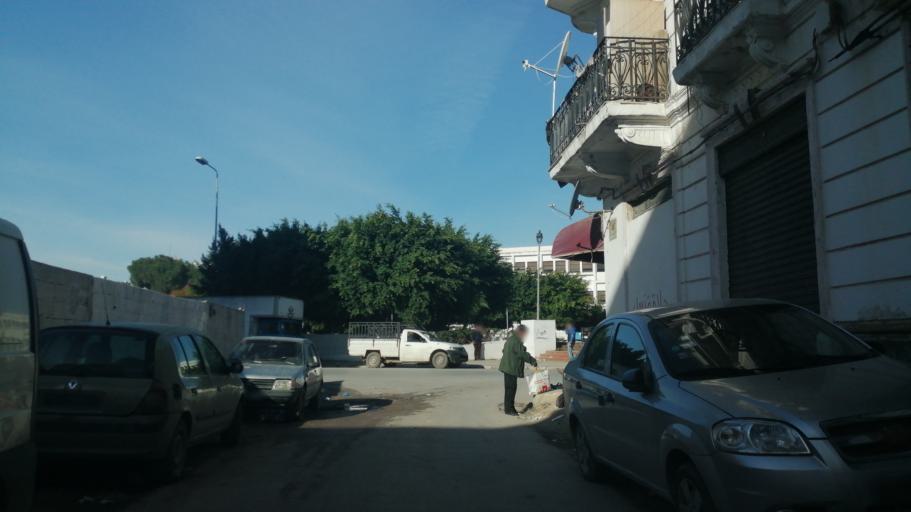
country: TN
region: Tunis
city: Tunis
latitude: 36.8099
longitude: 10.1746
